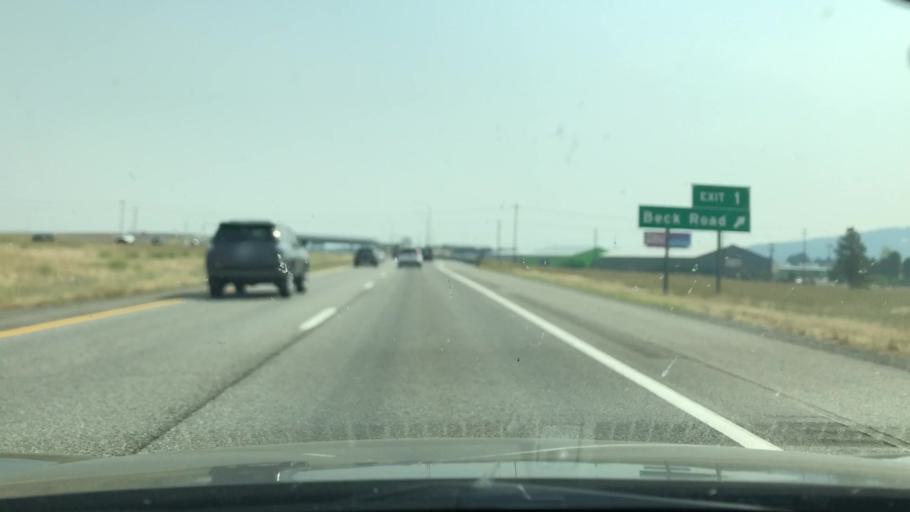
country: US
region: Washington
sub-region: Spokane County
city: Otis Orchards-East Farms
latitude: 47.6991
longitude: -117.0263
